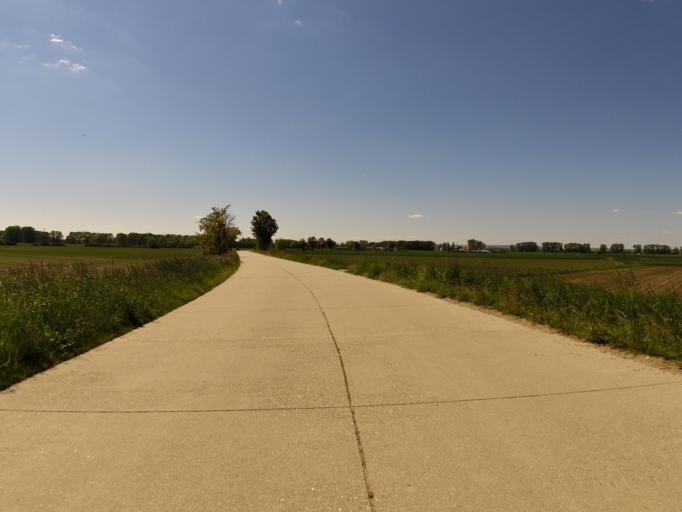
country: DE
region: Rheinland-Pfalz
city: Worms
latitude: 49.6842
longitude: 8.3802
